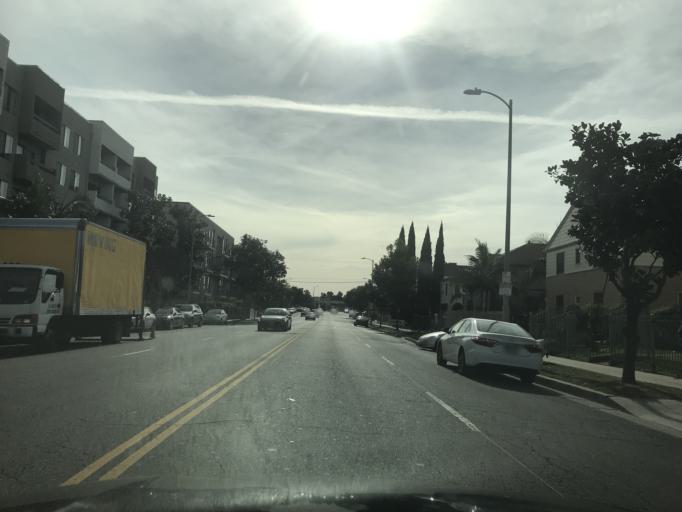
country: US
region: California
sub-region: Los Angeles County
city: Hollywood
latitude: 34.0555
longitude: -118.3143
